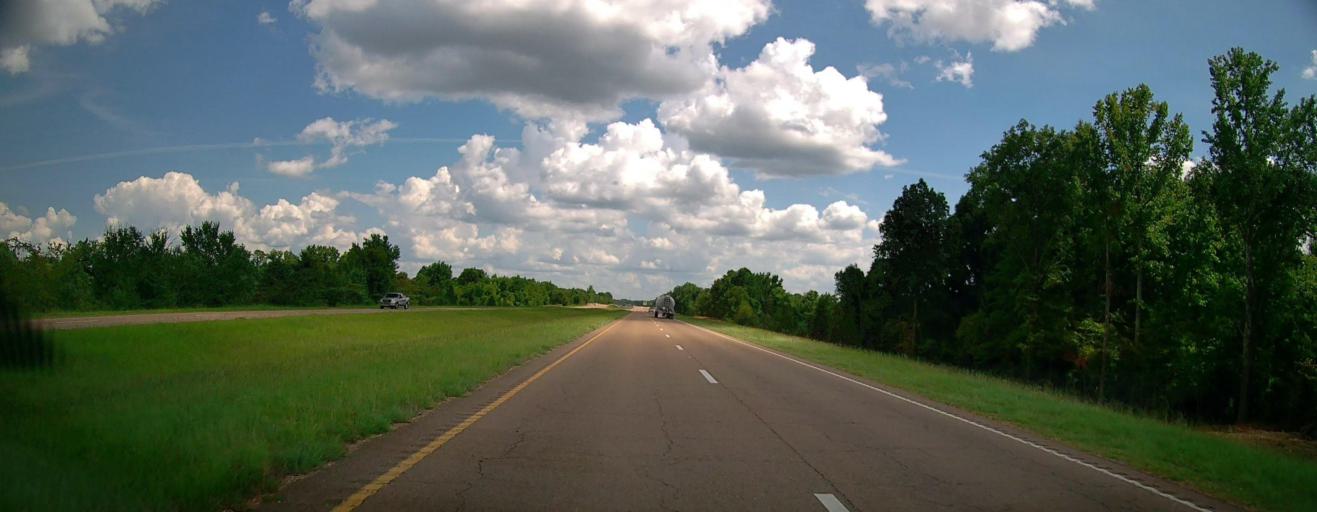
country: US
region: Mississippi
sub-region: Lowndes County
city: Columbus Air Force Base
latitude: 33.6786
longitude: -88.4320
